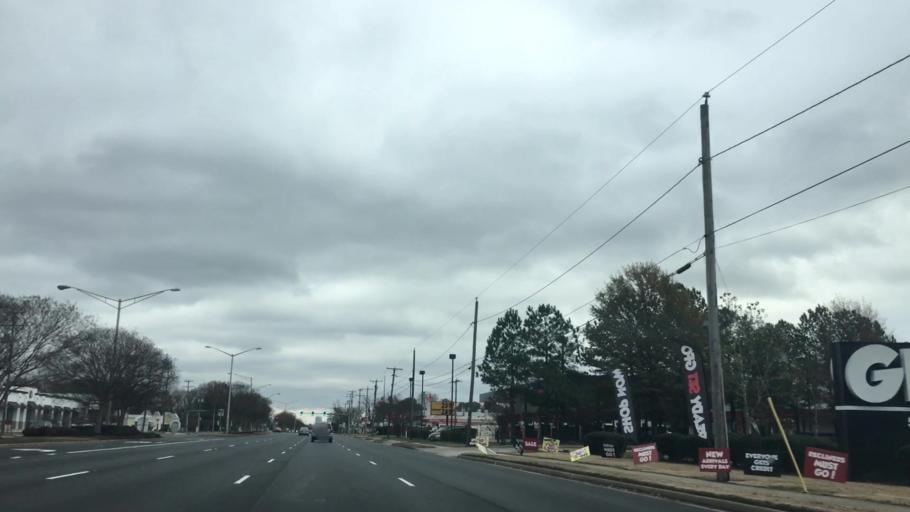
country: US
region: Virginia
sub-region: City of Chesapeake
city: Chesapeake
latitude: 36.8530
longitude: -76.1748
